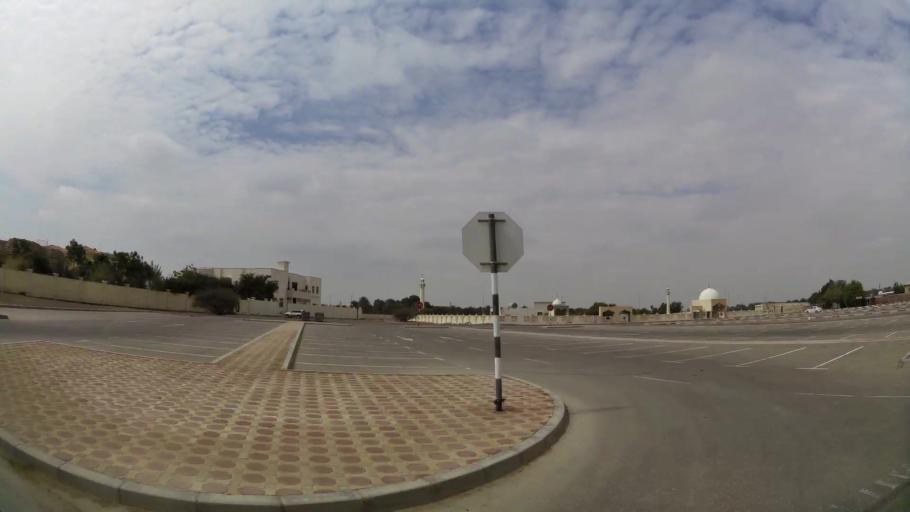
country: OM
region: Al Buraimi
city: Al Buraymi
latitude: 24.2142
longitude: 55.7956
